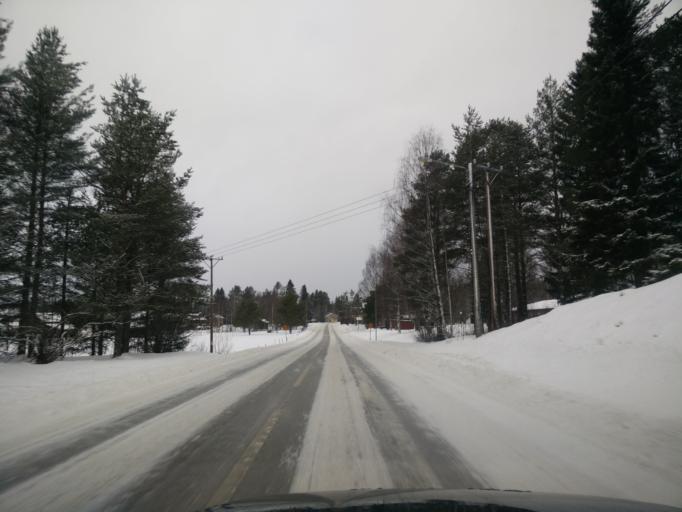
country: SE
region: Jaemtland
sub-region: Braecke Kommun
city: Braecke
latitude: 62.3967
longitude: 15.2151
